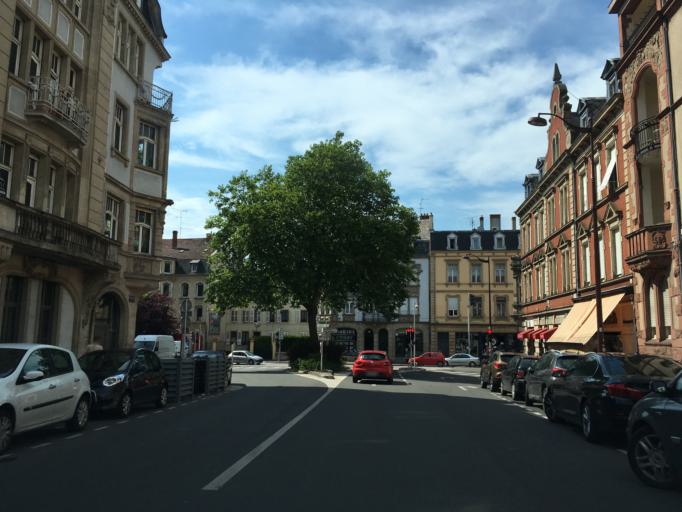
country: FR
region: Lorraine
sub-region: Departement de la Moselle
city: Montigny-les-Metz
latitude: 49.1030
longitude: 6.1624
